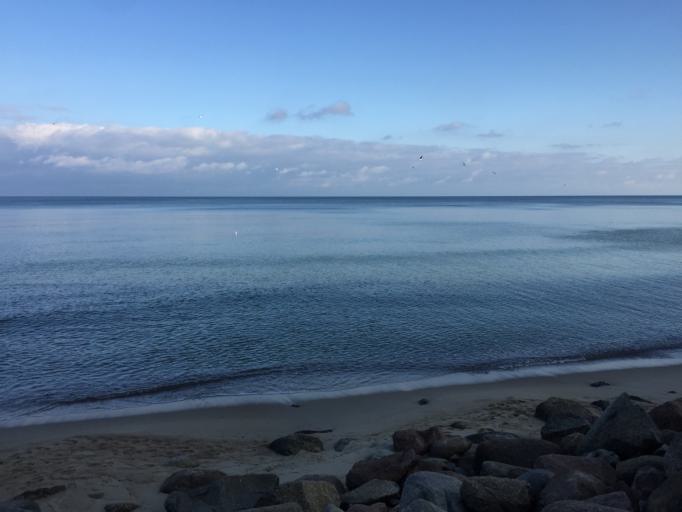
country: RU
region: Kaliningrad
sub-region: Gorod Svetlogorsk
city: Svetlogorsk
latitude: 54.9457
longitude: 20.1453
